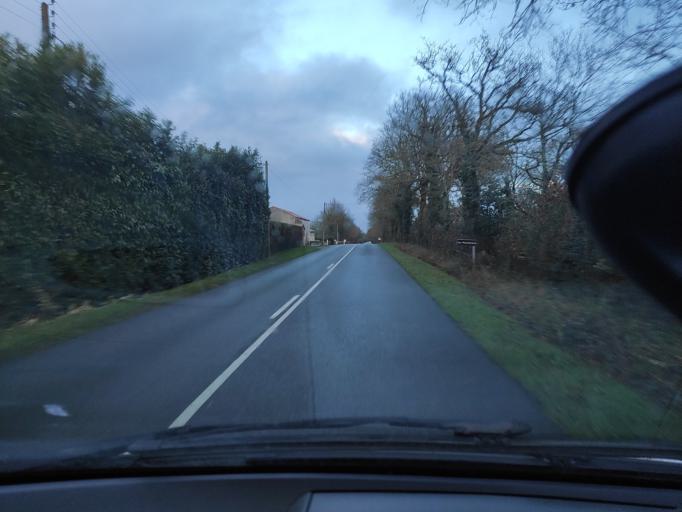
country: FR
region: Pays de la Loire
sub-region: Departement de la Vendee
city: Aubigny
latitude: 46.5911
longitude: -1.4698
